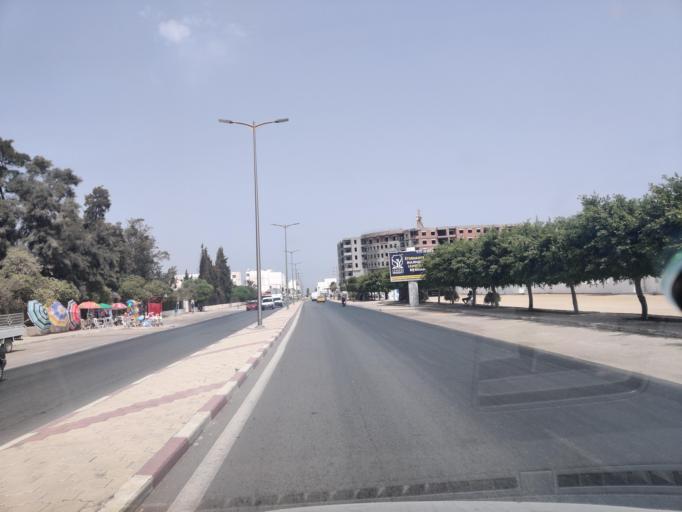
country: TN
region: Nabul
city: Bu `Urqub
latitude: 36.5927
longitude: 10.5031
